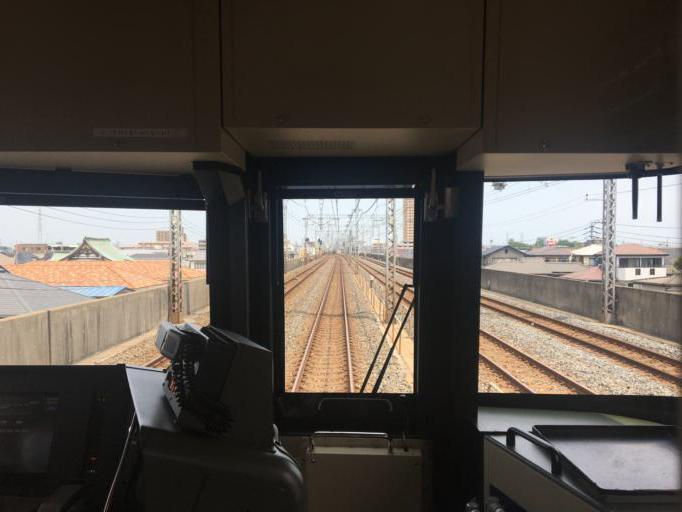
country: JP
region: Saitama
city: Koshigaya
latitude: 35.8963
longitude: 139.7822
